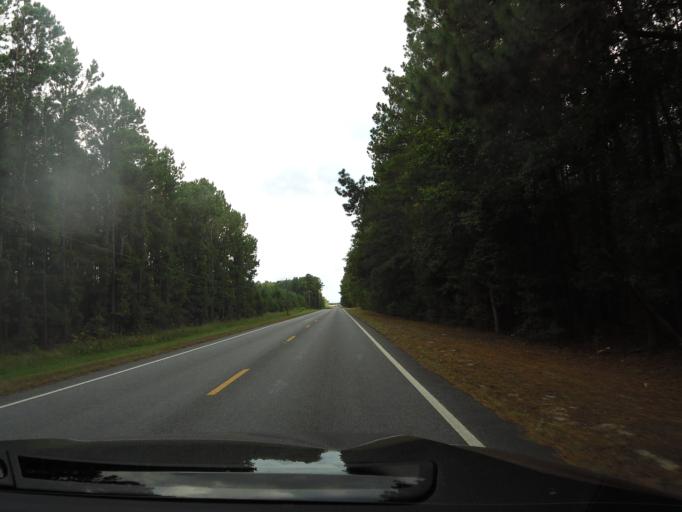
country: US
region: Georgia
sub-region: Liberty County
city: Midway
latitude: 31.6687
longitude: -81.4006
